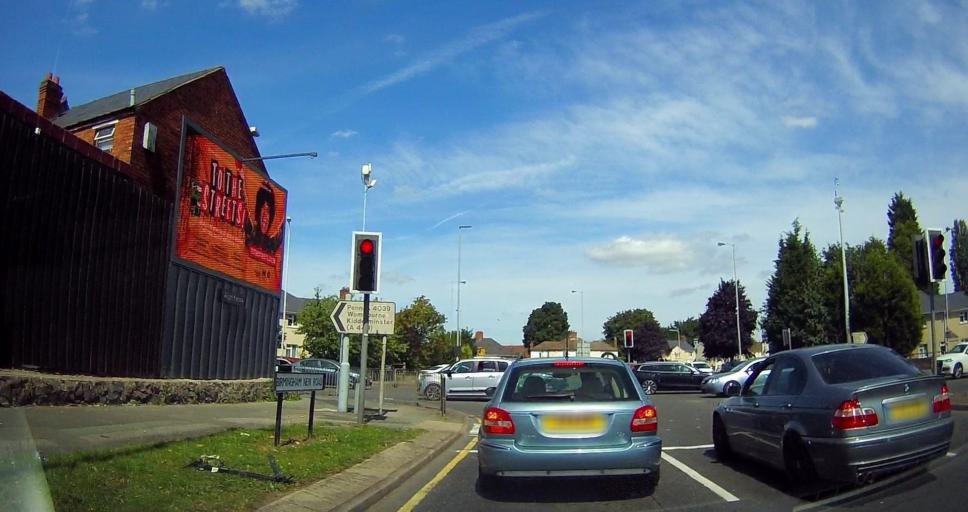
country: GB
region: England
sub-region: Wolverhampton
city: Wolverhampton
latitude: 52.5666
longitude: -2.1159
